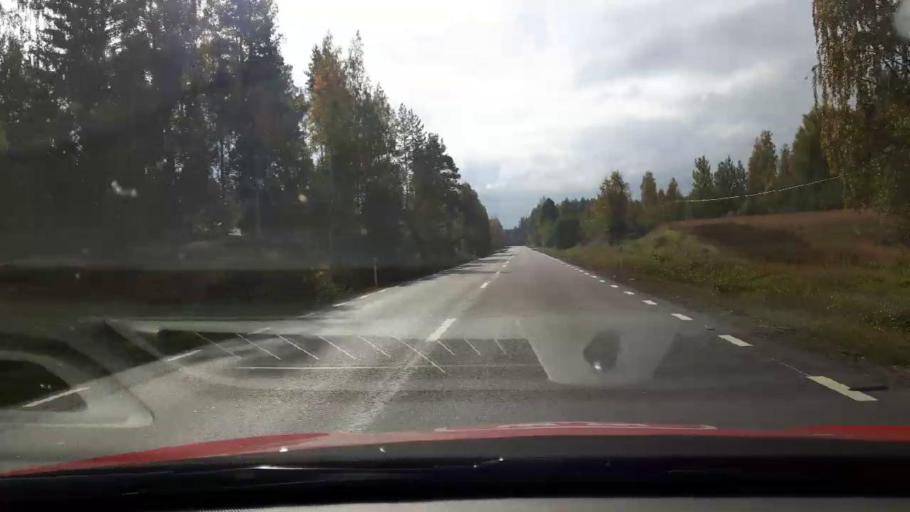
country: SE
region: Gaevleborg
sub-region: Bollnas Kommun
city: Arbra
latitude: 61.4781
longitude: 16.3646
